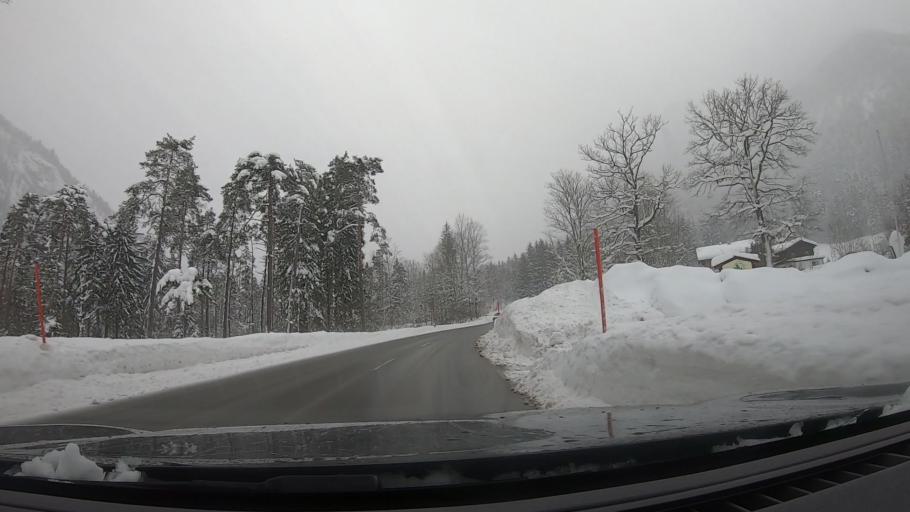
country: DE
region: Bavaria
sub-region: Upper Bavaria
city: Ruhpolding
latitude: 47.7316
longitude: 12.6636
